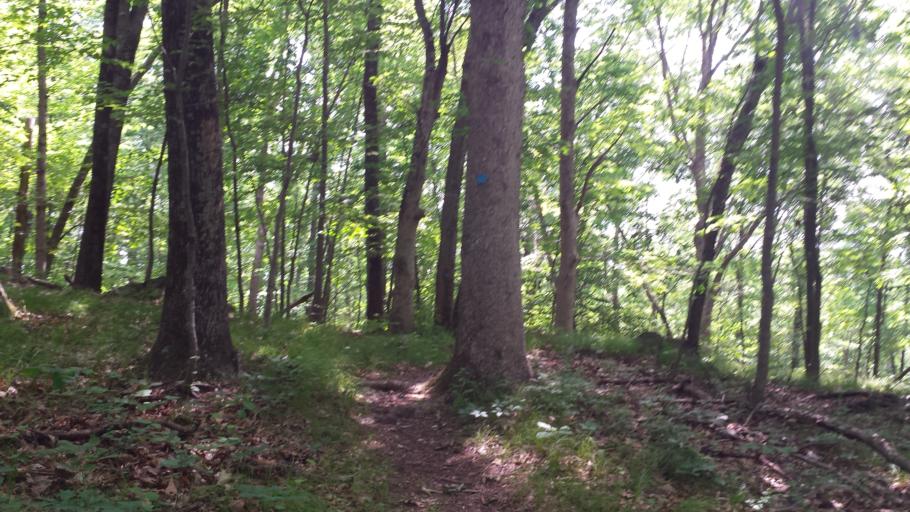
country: US
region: New York
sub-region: Westchester County
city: Yorktown Heights
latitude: 41.2645
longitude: -73.7370
